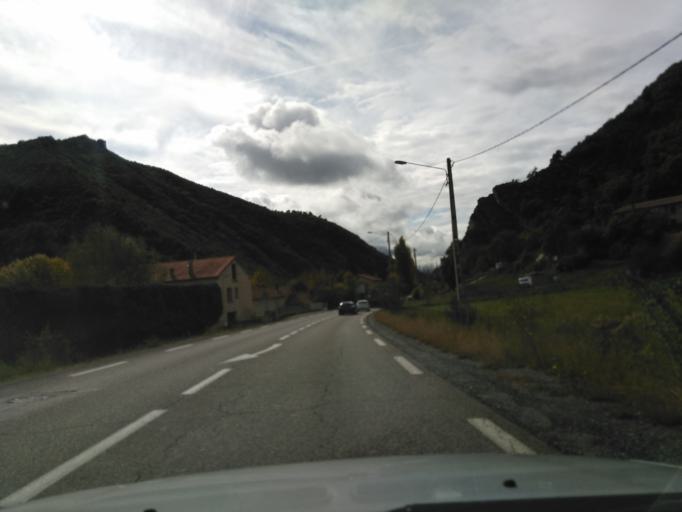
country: FR
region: Provence-Alpes-Cote d'Azur
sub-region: Departement des Alpes-de-Haute-Provence
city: Digne-les-Bains
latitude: 44.1023
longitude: 6.2524
